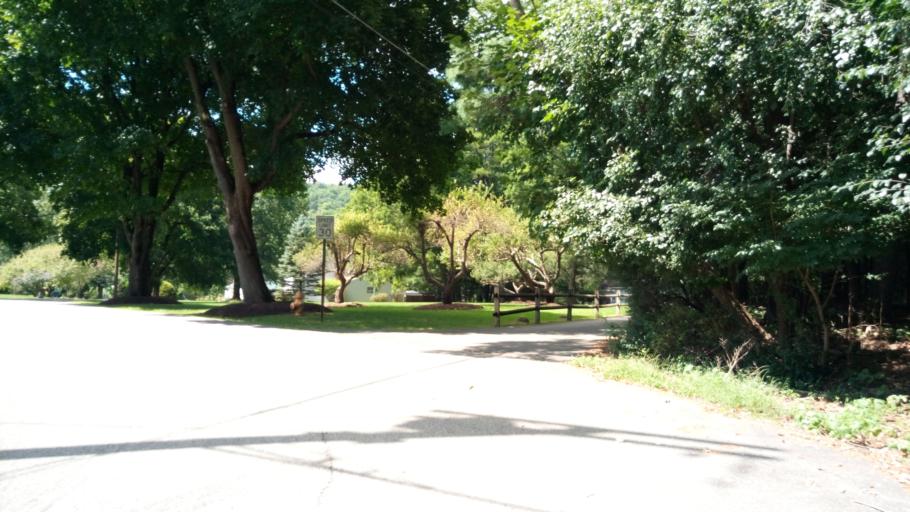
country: US
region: New York
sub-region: Chemung County
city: West Elmira
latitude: 42.0886
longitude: -76.8318
